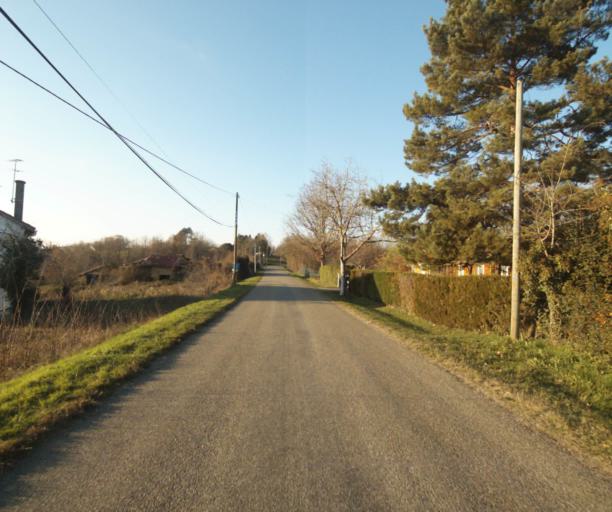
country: FR
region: Midi-Pyrenees
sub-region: Departement du Tarn-et-Garonne
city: Moissac
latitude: 44.1367
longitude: 1.1233
